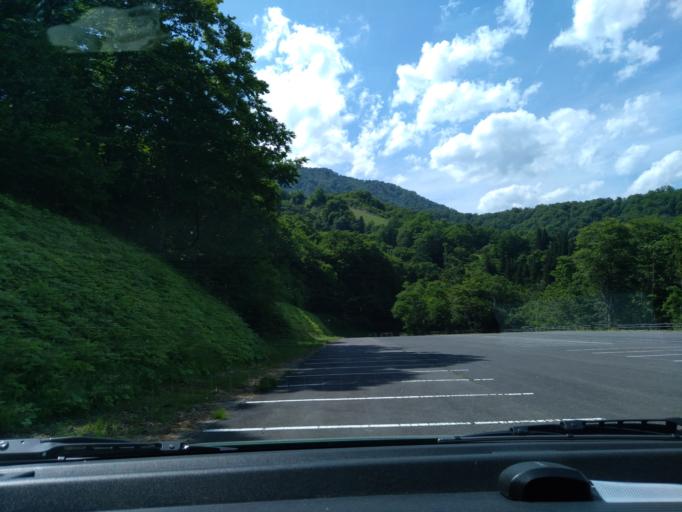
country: JP
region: Iwate
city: Ichinoseki
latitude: 39.0123
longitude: 140.8623
